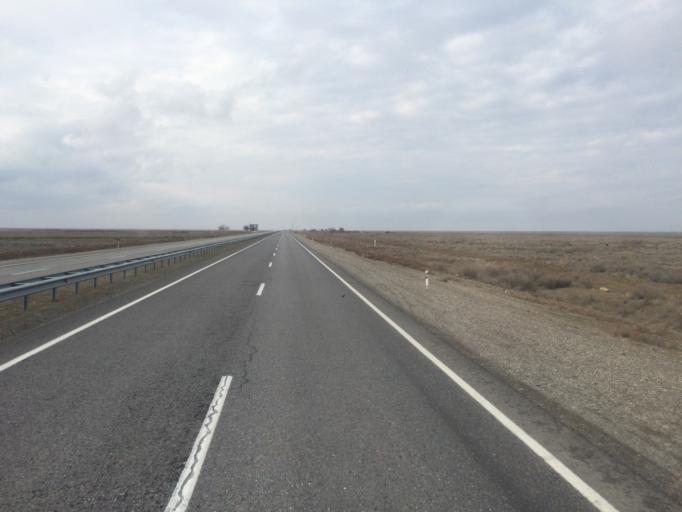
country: KZ
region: Ongtustik Qazaqstan
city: Turkestan
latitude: 43.5238
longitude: 67.7977
